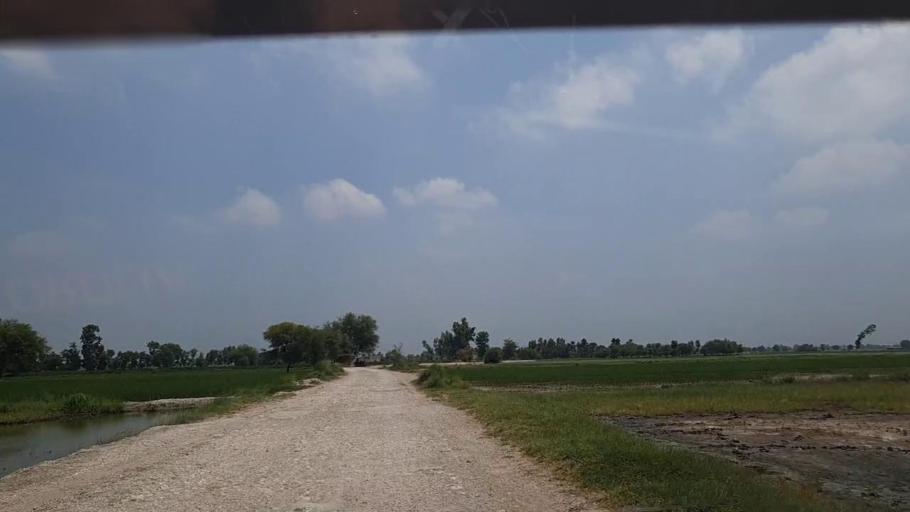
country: PK
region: Sindh
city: Khanpur
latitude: 27.8999
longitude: 69.3913
